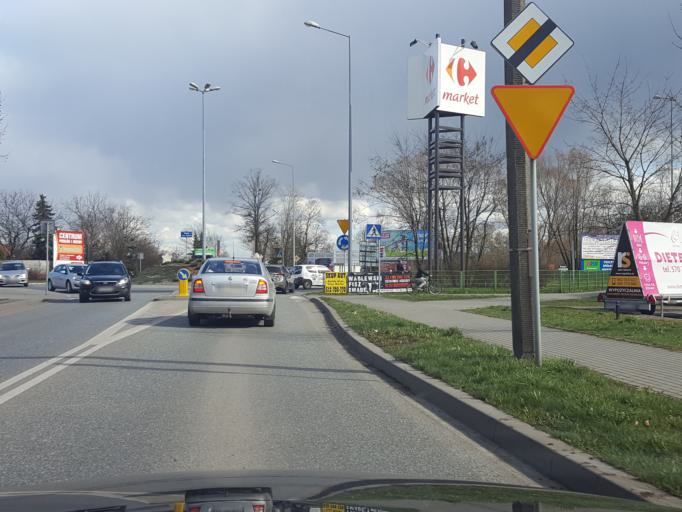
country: PL
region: Silesian Voivodeship
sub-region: Powiat pszczynski
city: Pszczyna
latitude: 49.9700
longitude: 18.9463
